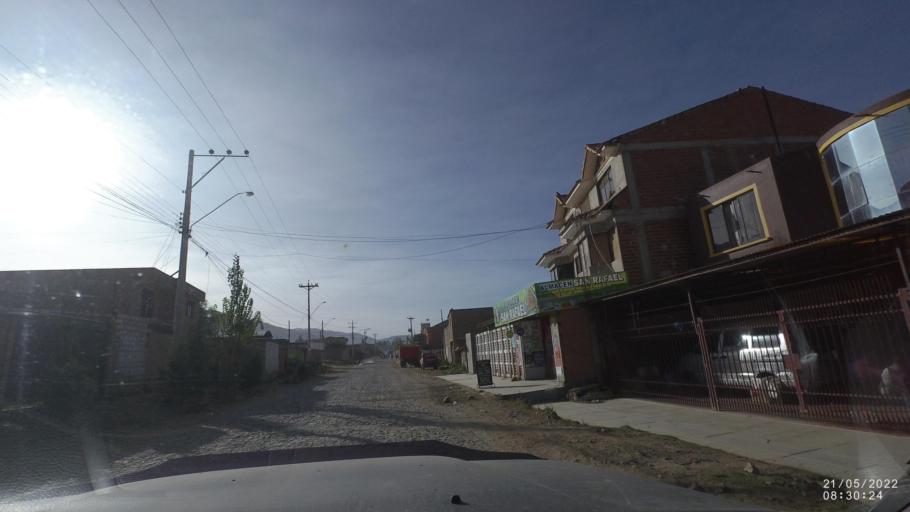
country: BO
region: Cochabamba
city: Cochabamba
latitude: -17.3847
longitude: -66.0591
